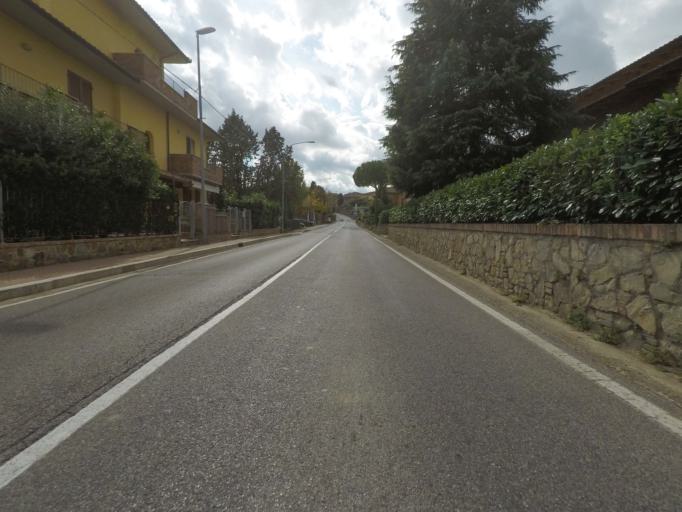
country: IT
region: Tuscany
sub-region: Provincia di Siena
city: Torrita di Siena
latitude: 43.1709
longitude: 11.7743
